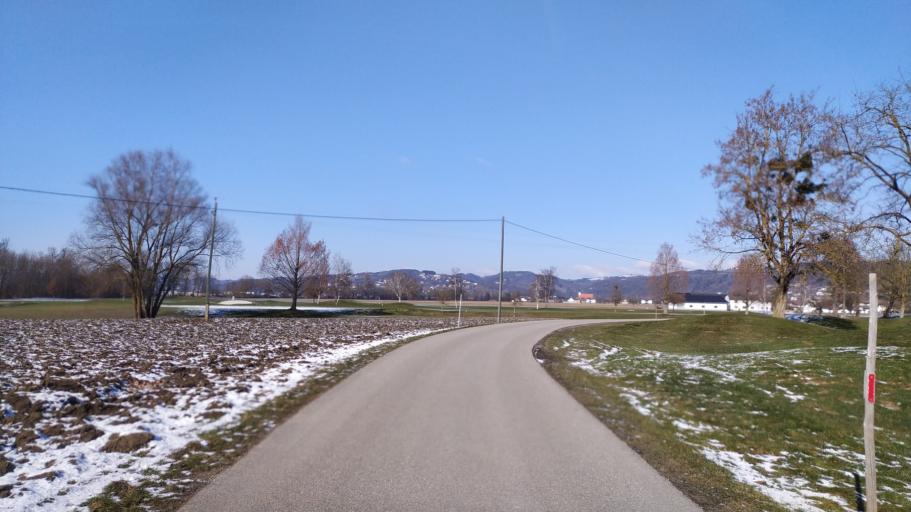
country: AT
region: Upper Austria
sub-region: Politischer Bezirk Urfahr-Umgebung
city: Goldworth
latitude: 48.3364
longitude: 14.0780
